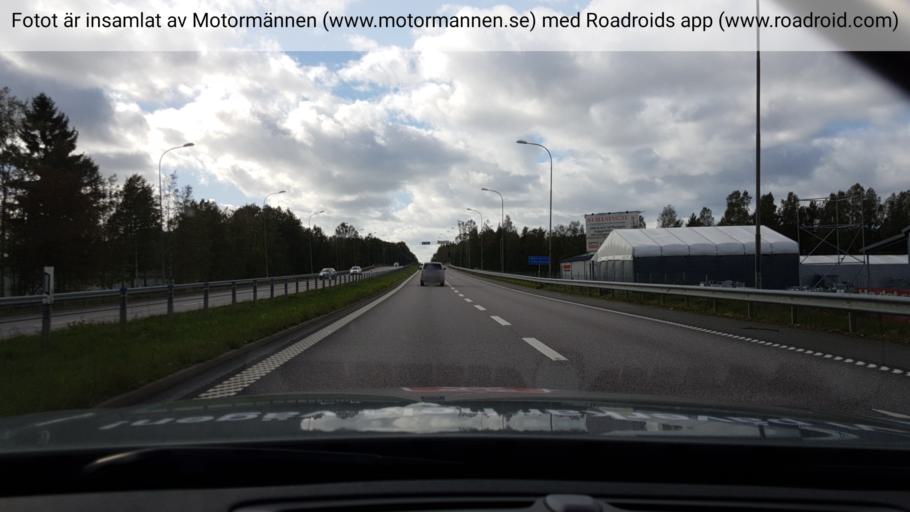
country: SE
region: OErebro
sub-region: Karlskoga Kommun
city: Karlskoga
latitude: 59.3235
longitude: 14.4871
